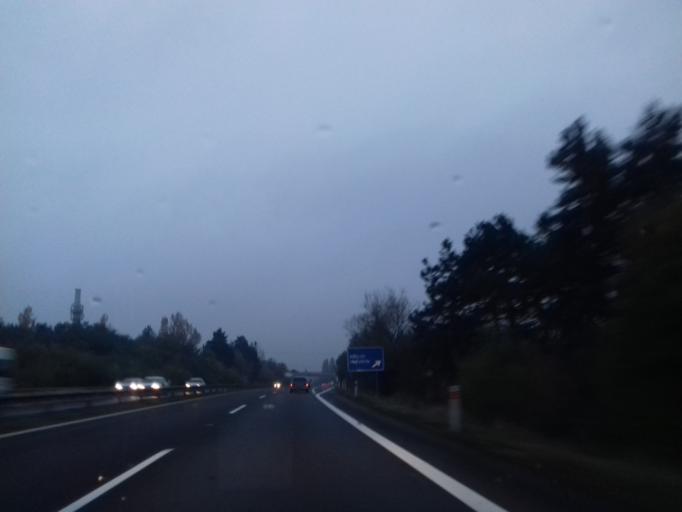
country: CZ
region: Olomoucky
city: Horka nad Moravou
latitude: 49.6115
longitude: 17.1939
